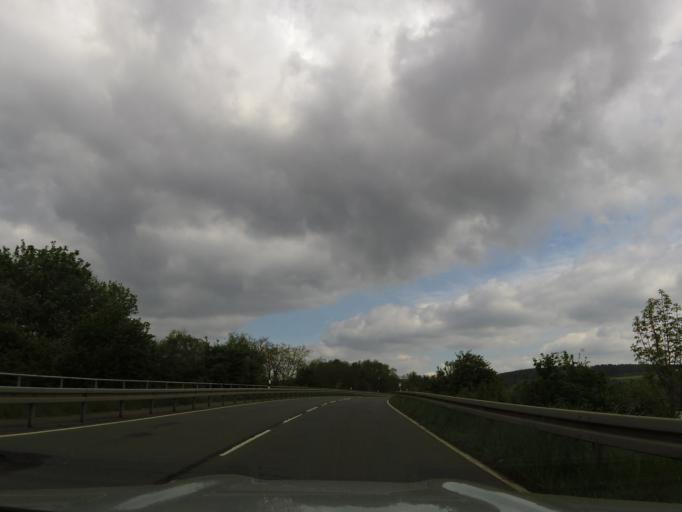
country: DE
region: Hesse
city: Burgsolms
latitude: 50.5441
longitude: 8.4087
